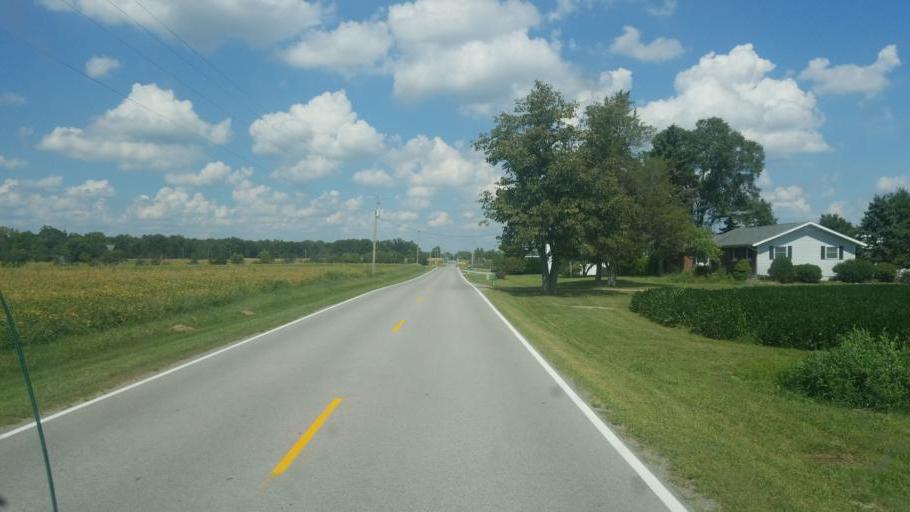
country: US
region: Ohio
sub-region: Hancock County
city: Arlington
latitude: 40.8869
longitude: -83.7271
